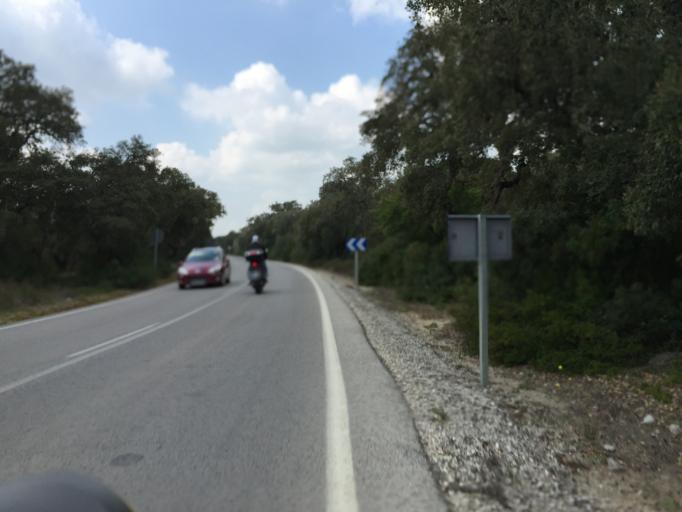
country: ES
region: Andalusia
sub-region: Provincia de Cadiz
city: Vejer de la Frontera
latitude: 36.2961
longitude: -5.9180
